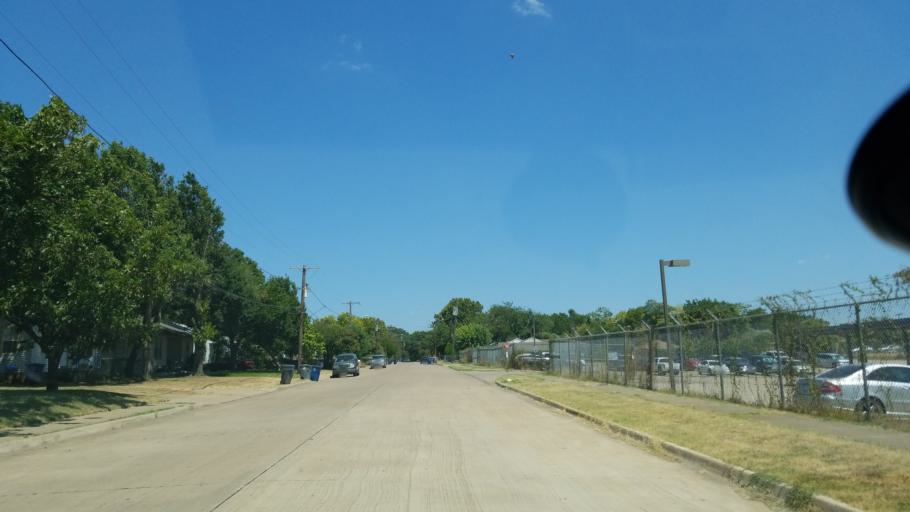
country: US
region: Texas
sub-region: Dallas County
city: Cockrell Hill
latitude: 32.7224
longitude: -96.8906
